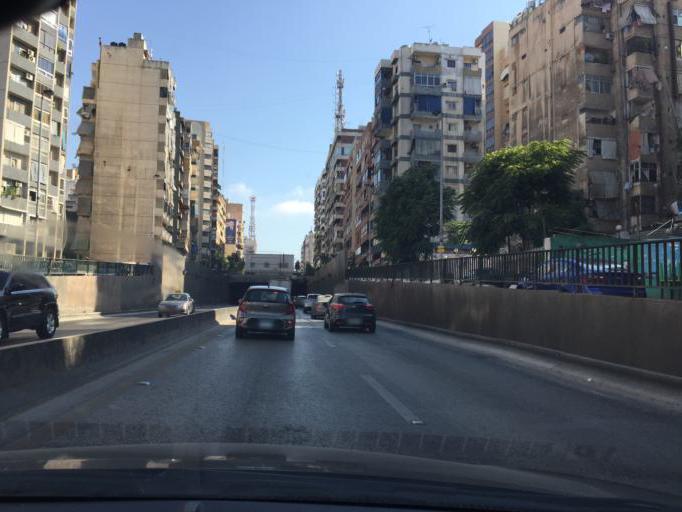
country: LB
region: Beyrouth
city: Beirut
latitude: 33.8886
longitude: 35.4995
